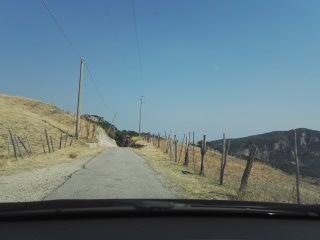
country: IT
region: Calabria
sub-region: Provincia di Reggio Calabria
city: Stilo
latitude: 38.4501
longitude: 16.4628
